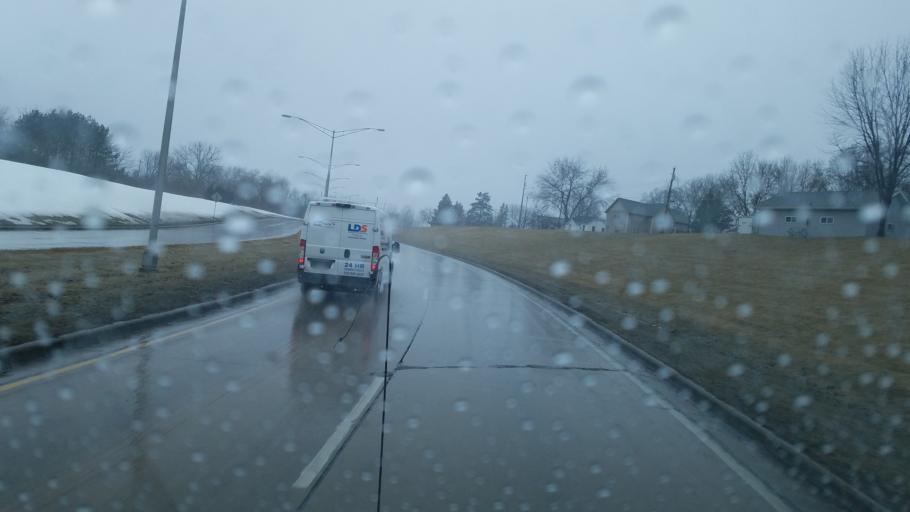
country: US
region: Wisconsin
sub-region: Wood County
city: Marshfield
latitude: 44.6715
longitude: -90.1829
